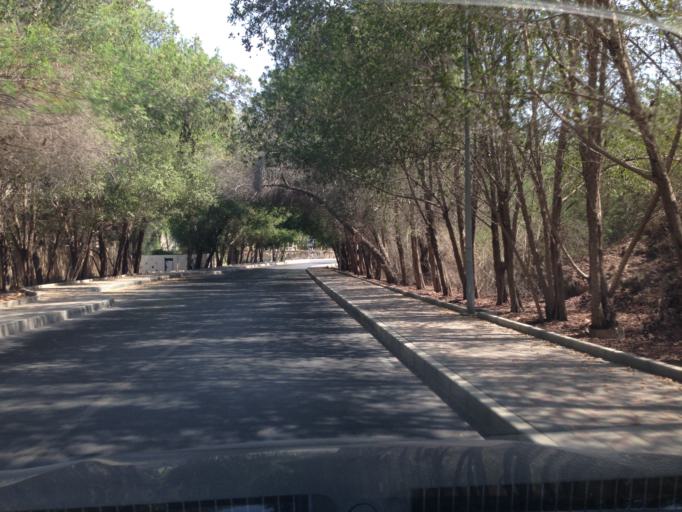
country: OM
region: Muhafazat Masqat
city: Muscat
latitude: 23.6294
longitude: 58.4846
